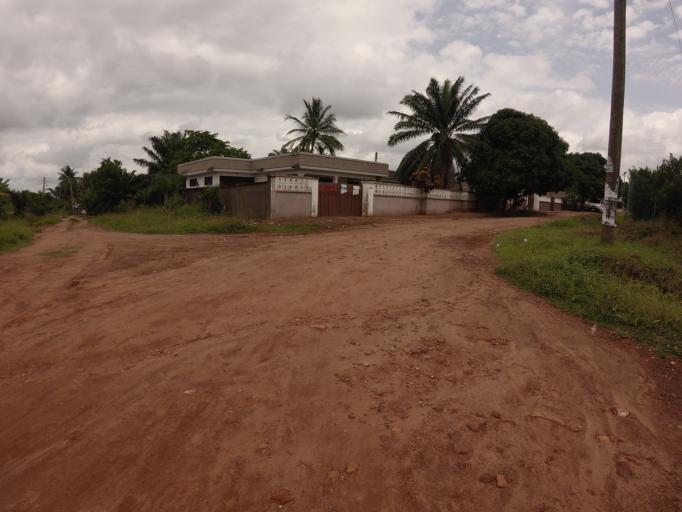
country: GH
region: Volta
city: Ho
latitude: 6.5966
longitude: 0.4850
